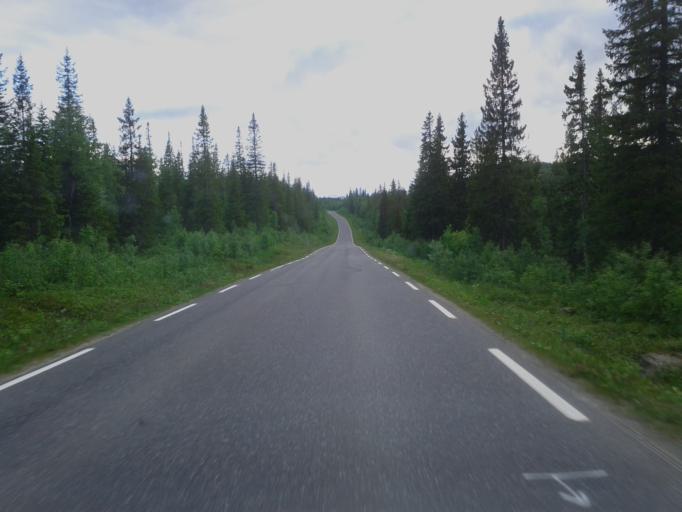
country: NO
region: Nordland
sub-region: Hattfjelldal
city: Hattfjelldal
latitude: 65.5574
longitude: 13.7505
